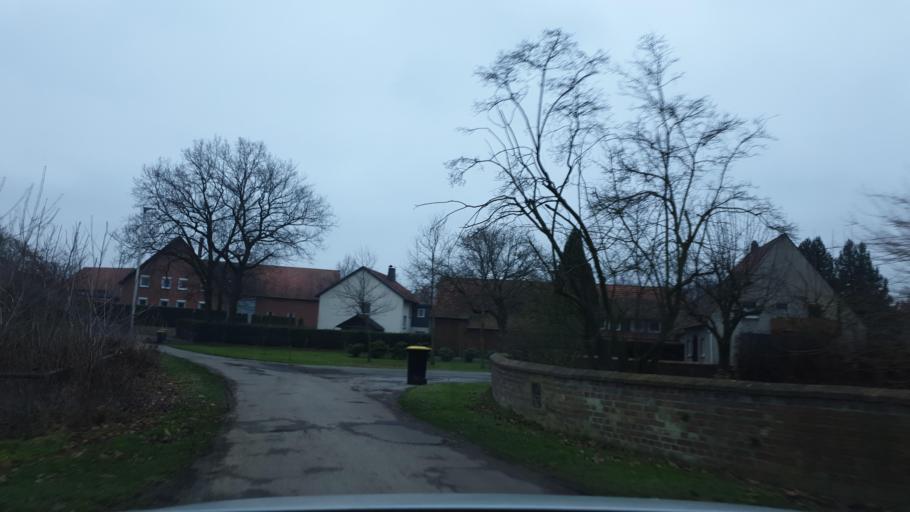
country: DE
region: North Rhine-Westphalia
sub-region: Regierungsbezirk Detmold
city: Hille
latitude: 52.2890
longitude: 8.7944
